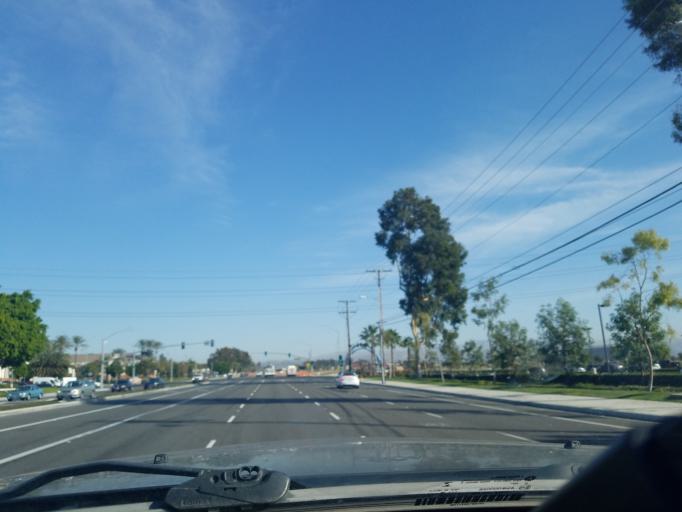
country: US
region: California
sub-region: Orange County
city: Irvine
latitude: 33.7046
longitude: -117.8441
